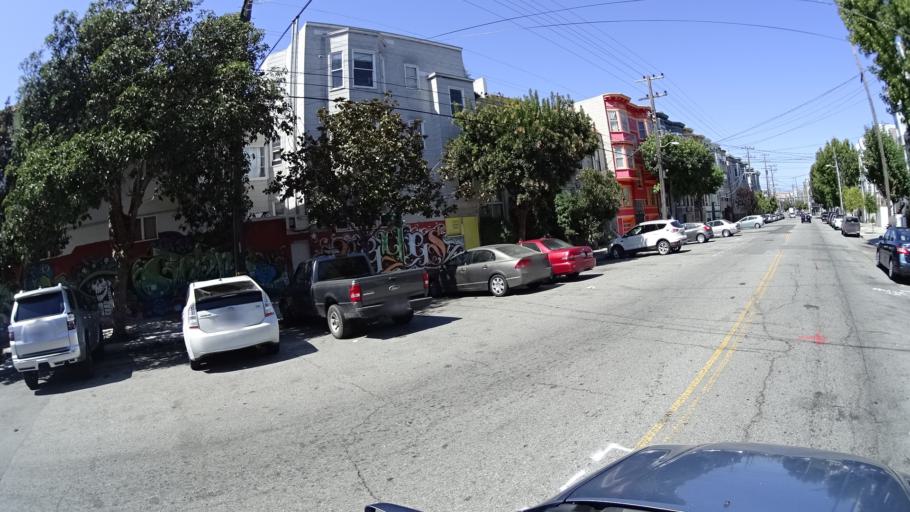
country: US
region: California
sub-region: San Francisco County
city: San Francisco
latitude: 37.7578
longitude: -122.4096
